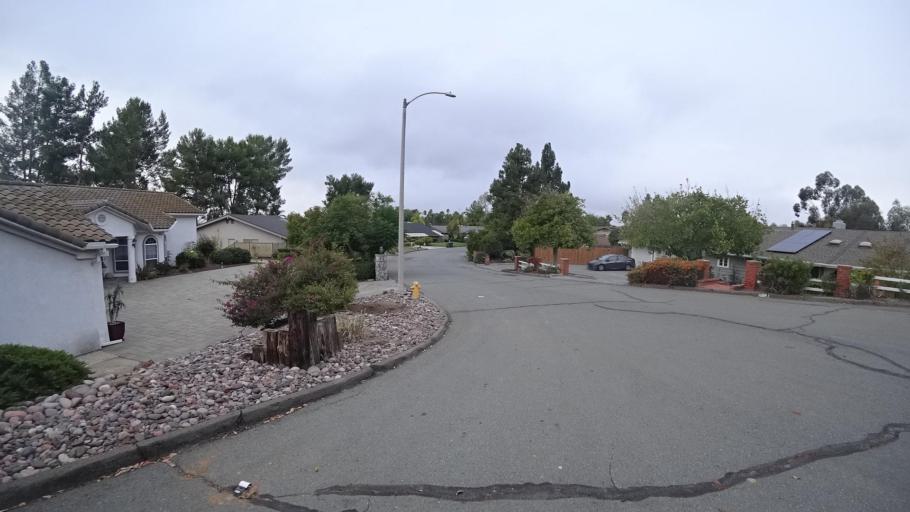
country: US
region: California
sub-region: San Diego County
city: Granite Hills
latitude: 32.7758
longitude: -116.9121
